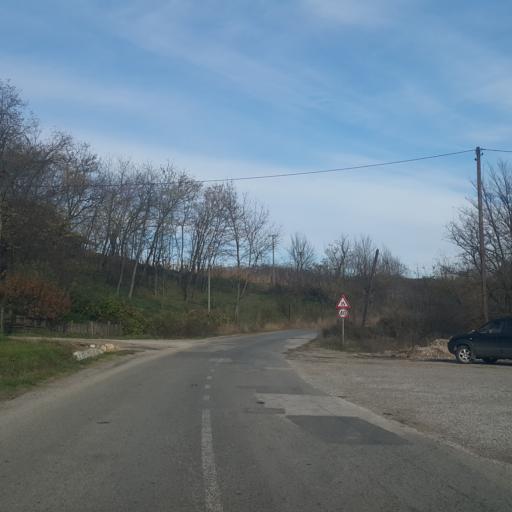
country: RS
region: Central Serbia
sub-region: Belgrade
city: Lazarevac
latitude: 44.3527
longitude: 20.4011
